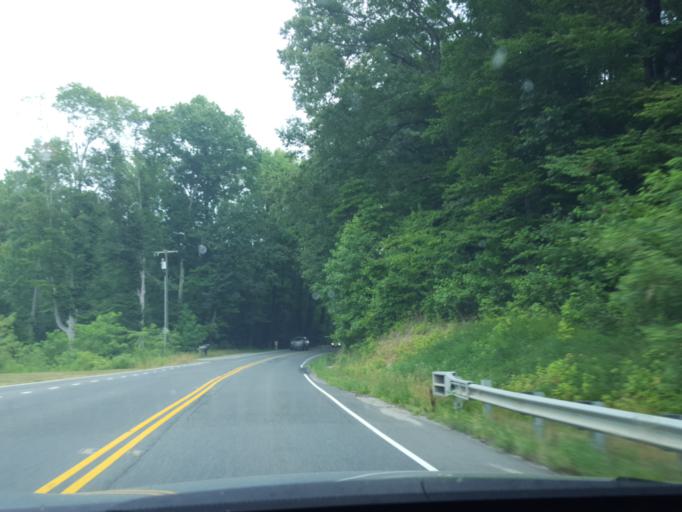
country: US
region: Virginia
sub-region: King George County
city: Dahlgren
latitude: 38.3405
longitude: -77.0825
